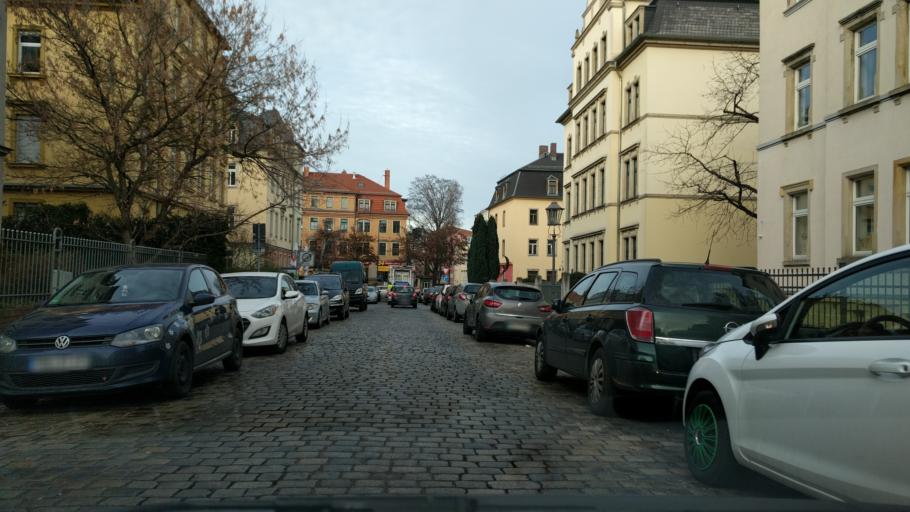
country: DE
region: Saxony
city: Dresden
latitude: 51.0421
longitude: 13.6925
